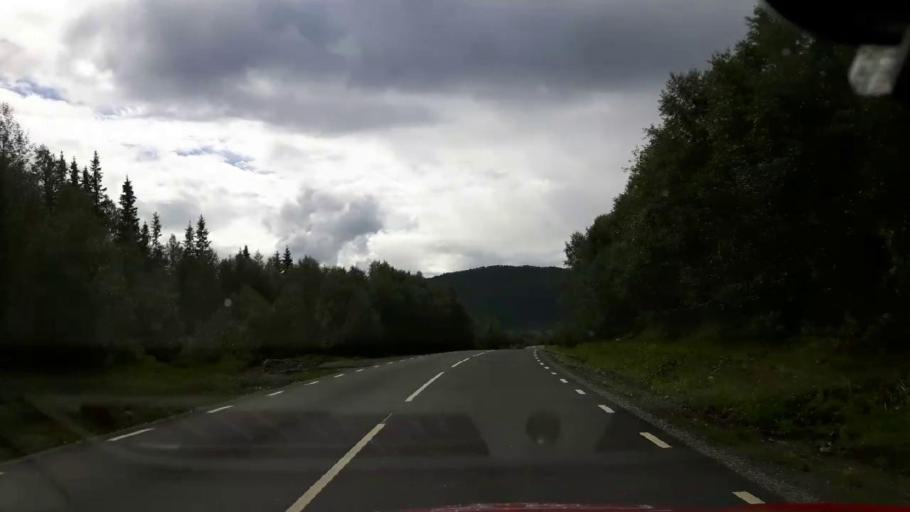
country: NO
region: Nord-Trondelag
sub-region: Royrvik
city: Royrvik
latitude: 64.8934
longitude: 14.1917
